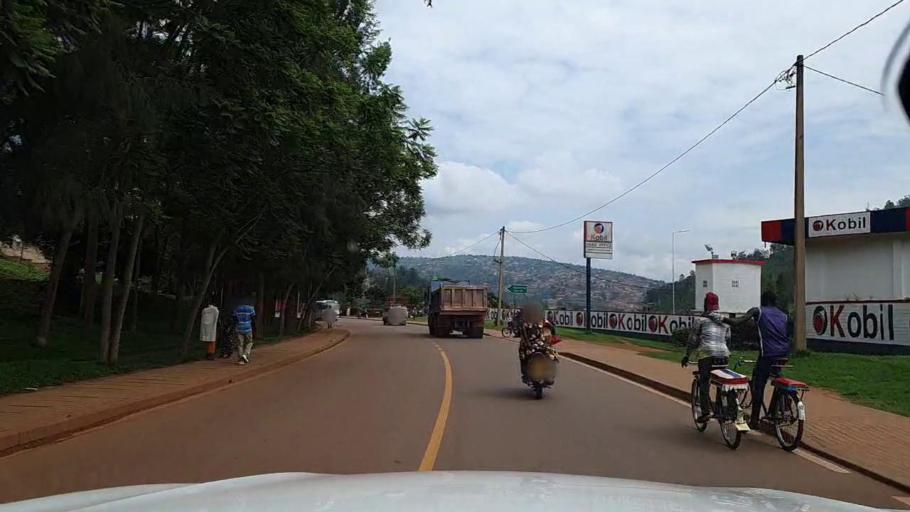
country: RW
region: Kigali
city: Kigali
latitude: -1.9187
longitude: 30.0480
